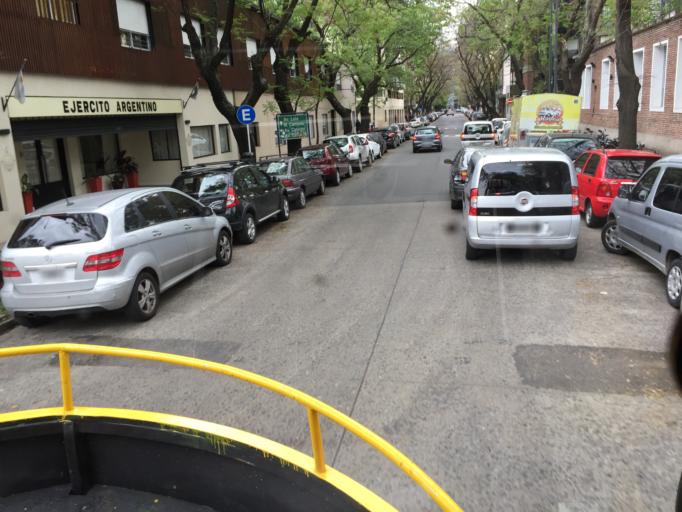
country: AR
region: Buenos Aires F.D.
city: Colegiales
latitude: -34.5739
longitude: -58.4301
